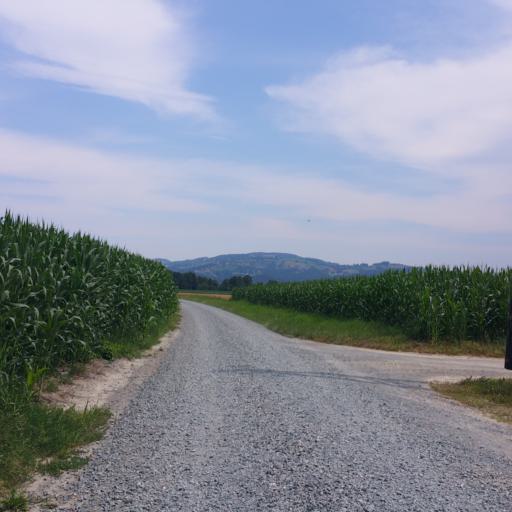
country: AT
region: Styria
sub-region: Politischer Bezirk Leibnitz
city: Gleinstatten
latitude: 46.7425
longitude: 15.3616
